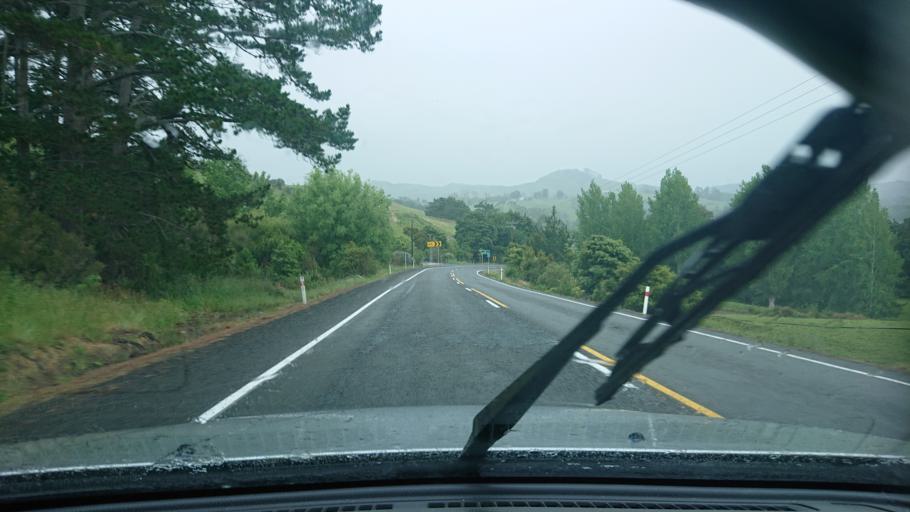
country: NZ
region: Auckland
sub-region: Auckland
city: Wellsford
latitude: -36.3123
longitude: 174.4948
